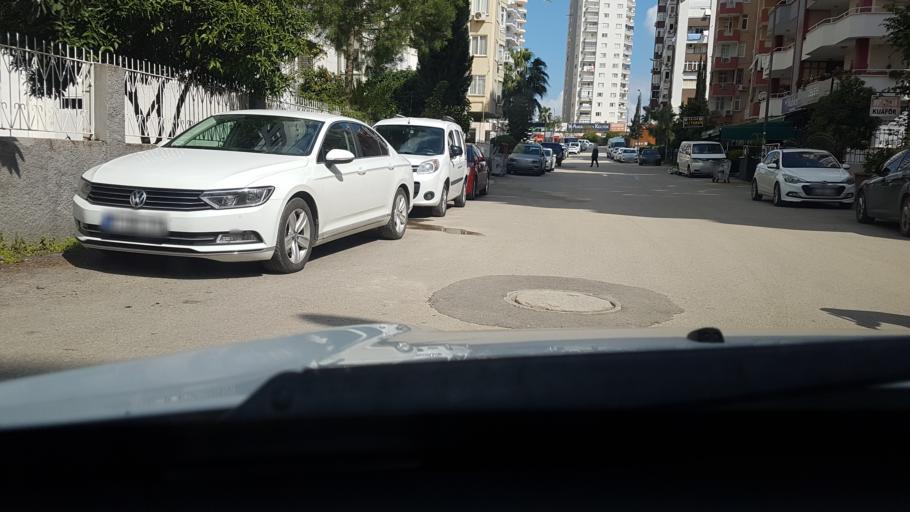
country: TR
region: Adana
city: Adana
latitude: 37.0449
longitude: 35.3028
